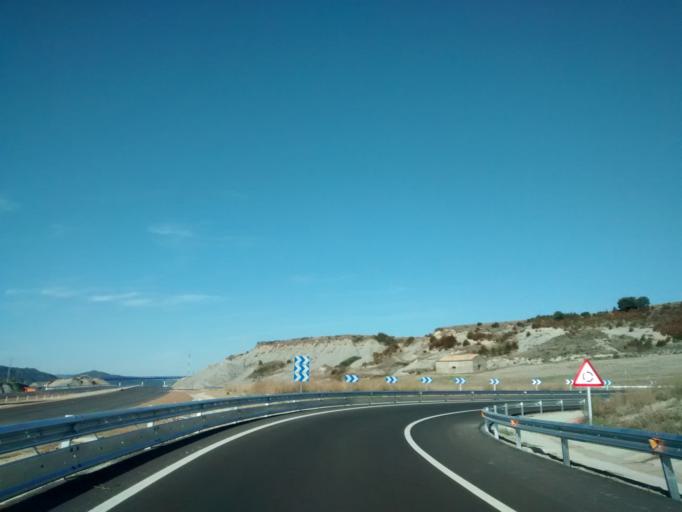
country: ES
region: Aragon
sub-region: Provincia de Huesca
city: Santa Cruz de la Seros
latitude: 42.5653
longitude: -0.7132
